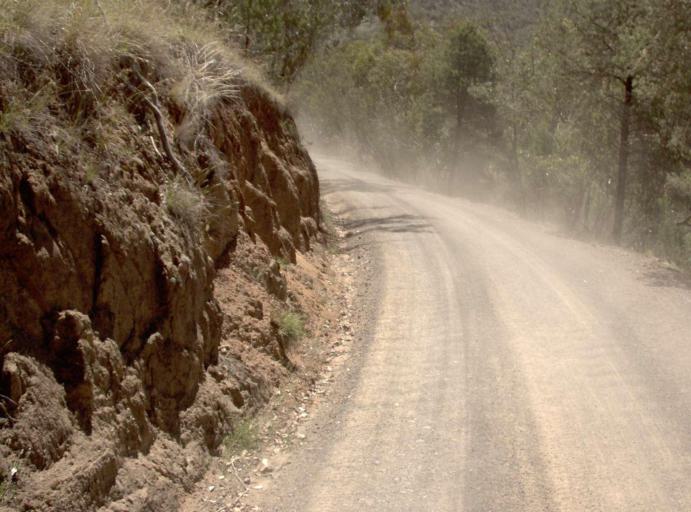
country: AU
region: New South Wales
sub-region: Snowy River
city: Jindabyne
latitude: -37.0797
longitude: 148.4592
